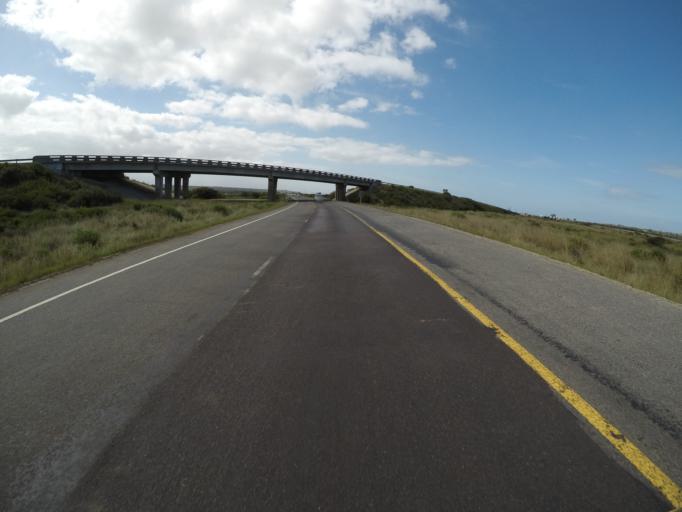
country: ZA
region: Western Cape
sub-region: Eden District Municipality
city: Mossel Bay
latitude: -34.1824
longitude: 22.0595
